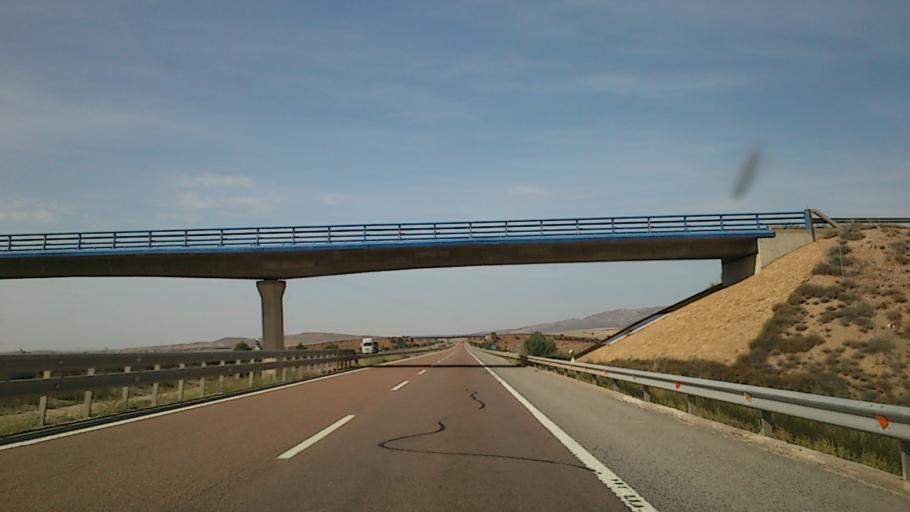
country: ES
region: Aragon
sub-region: Provincia de Teruel
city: Santa Eulalia
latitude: 40.5888
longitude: -1.2848
